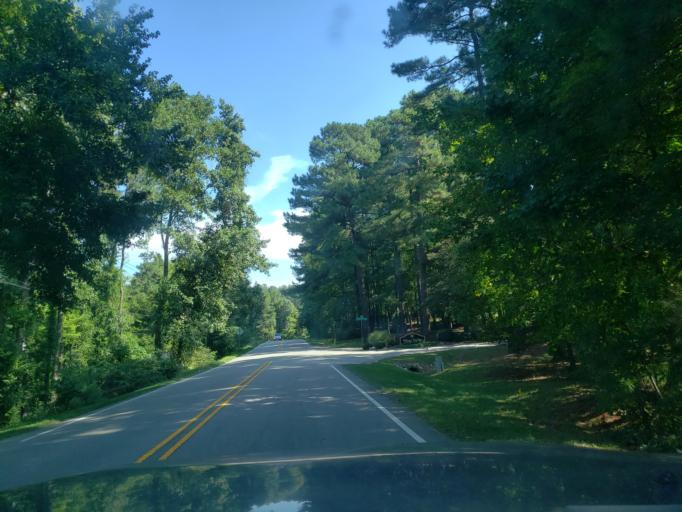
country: US
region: North Carolina
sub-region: Durham County
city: Gorman
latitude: 35.9309
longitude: -78.7195
